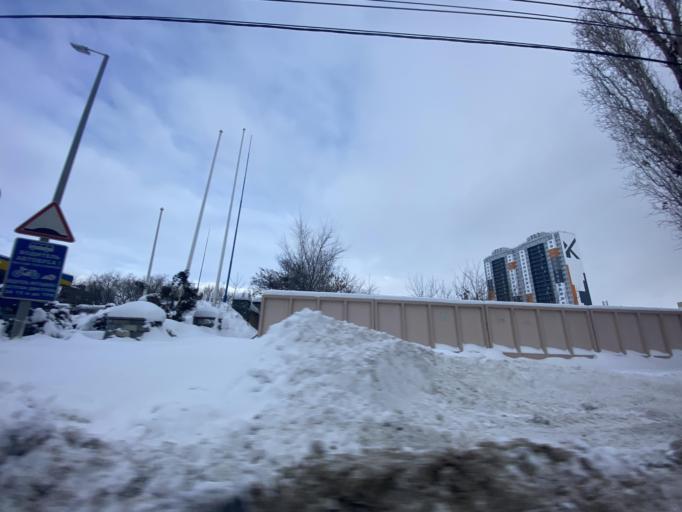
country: RU
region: Saratov
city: Engel's
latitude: 51.4998
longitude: 46.0855
